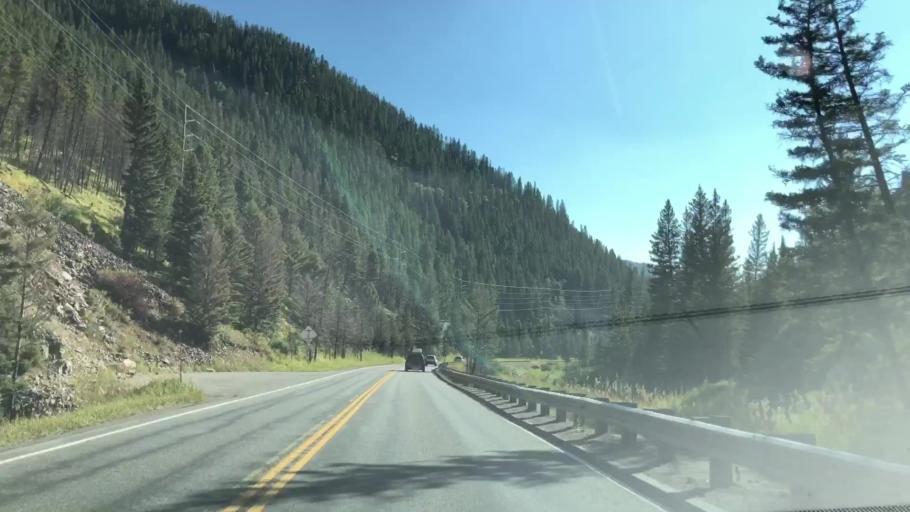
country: US
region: Montana
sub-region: Gallatin County
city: Big Sky
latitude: 45.3121
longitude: -111.1900
